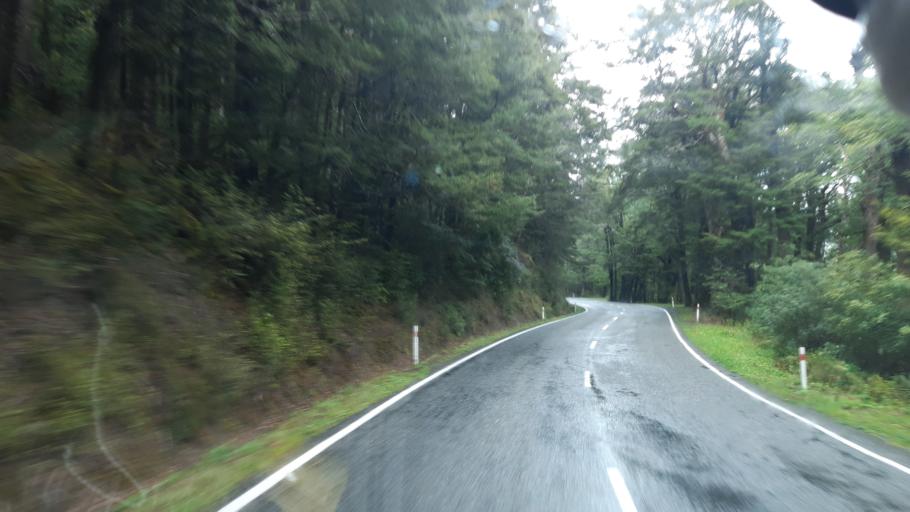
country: NZ
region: Canterbury
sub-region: Hurunui District
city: Amberley
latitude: -42.3765
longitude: 172.3582
